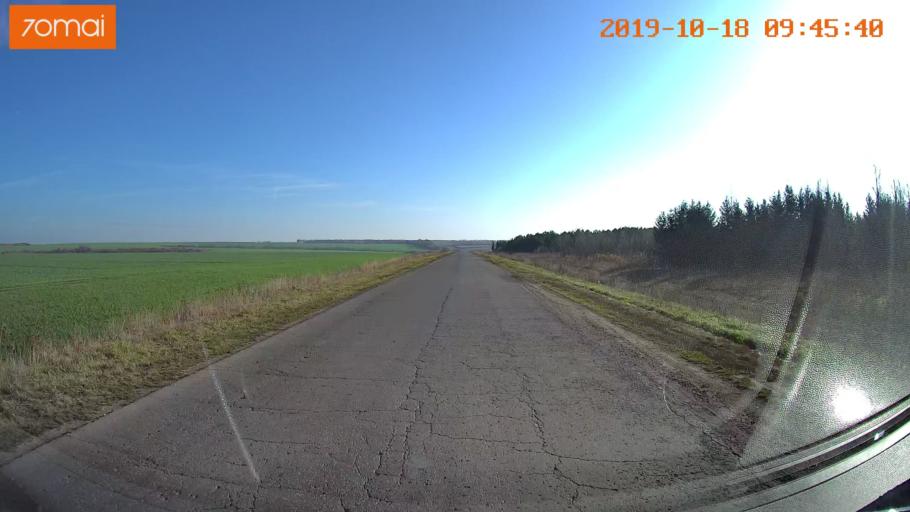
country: RU
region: Tula
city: Kazachka
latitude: 53.3126
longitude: 38.1953
